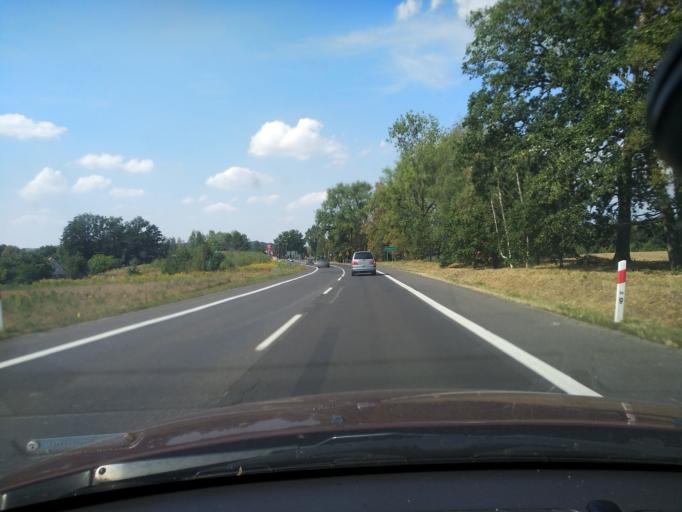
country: PL
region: Lower Silesian Voivodeship
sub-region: Powiat lubanski
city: Luban
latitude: 51.0979
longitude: 15.3122
